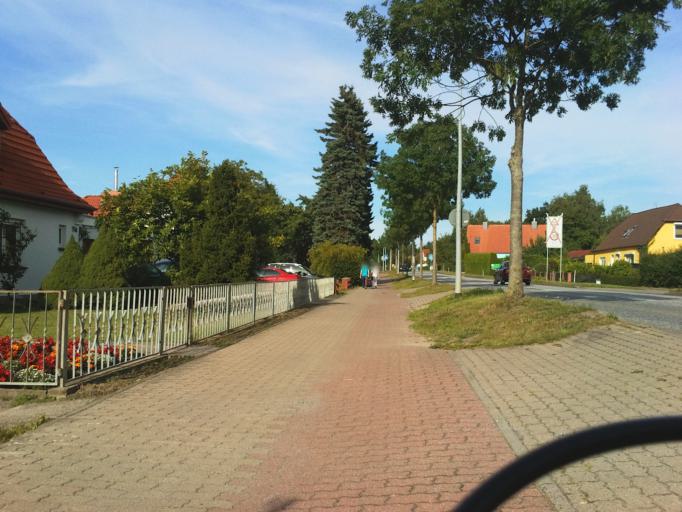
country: DE
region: Mecklenburg-Vorpommern
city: Kritzmow
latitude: 54.0684
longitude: 12.0781
